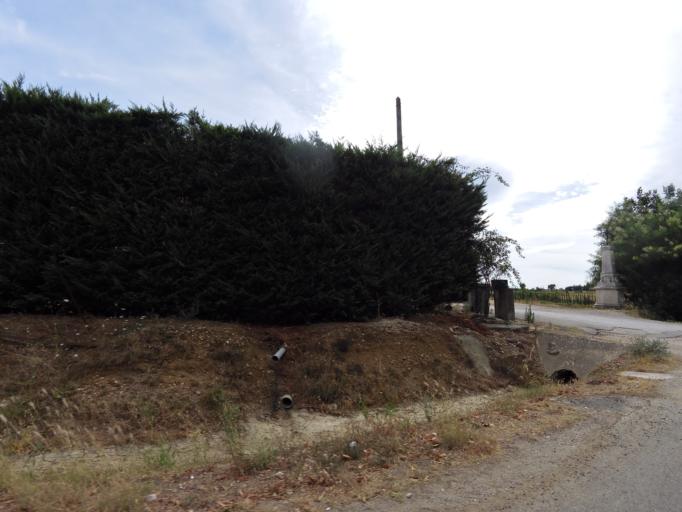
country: FR
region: Languedoc-Roussillon
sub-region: Departement du Gard
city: Saint-Mamert-du-Gard
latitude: 43.8848
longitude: 4.1899
